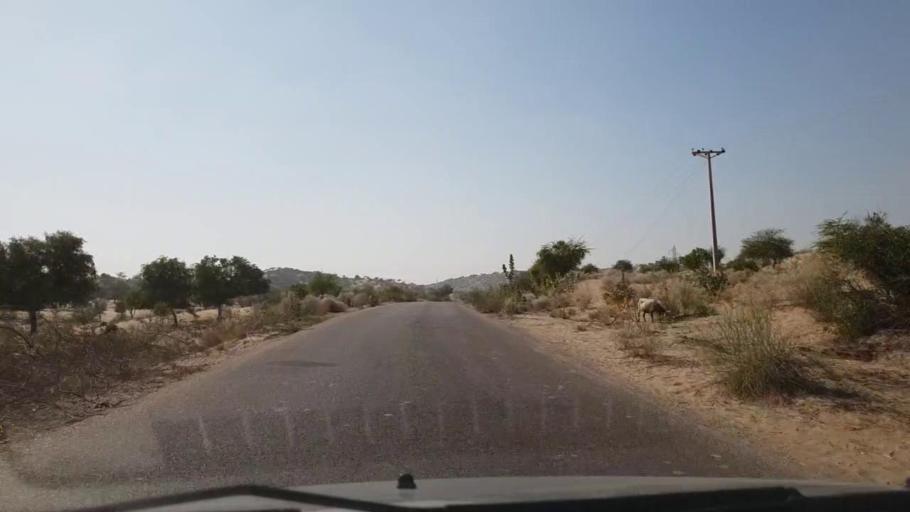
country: PK
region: Sindh
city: Diplo
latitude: 24.5612
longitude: 69.6710
